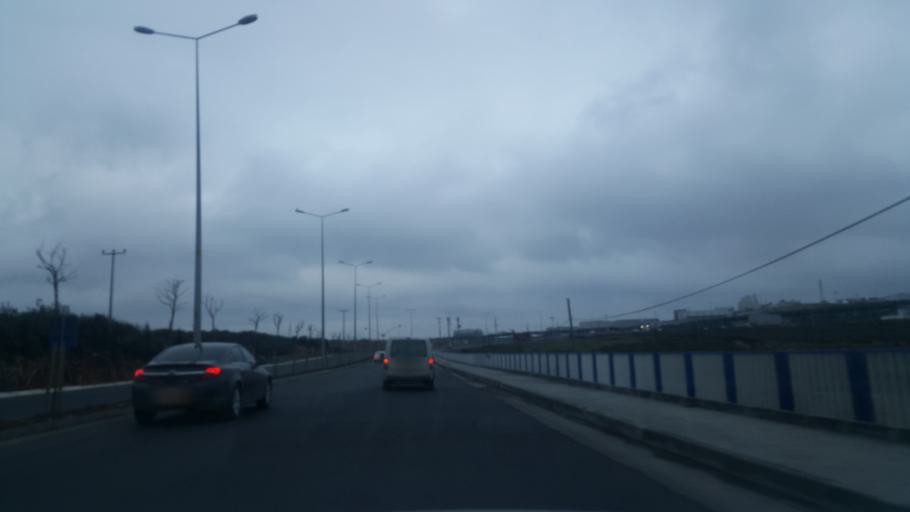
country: TR
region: Kocaeli
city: Tavsancil
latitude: 40.8015
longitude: 29.5518
